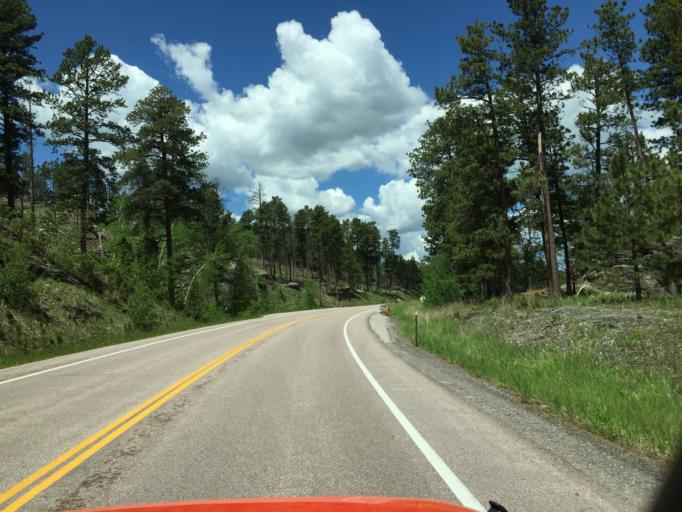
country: US
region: South Dakota
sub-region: Custer County
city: Custer
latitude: 43.8955
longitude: -103.5172
